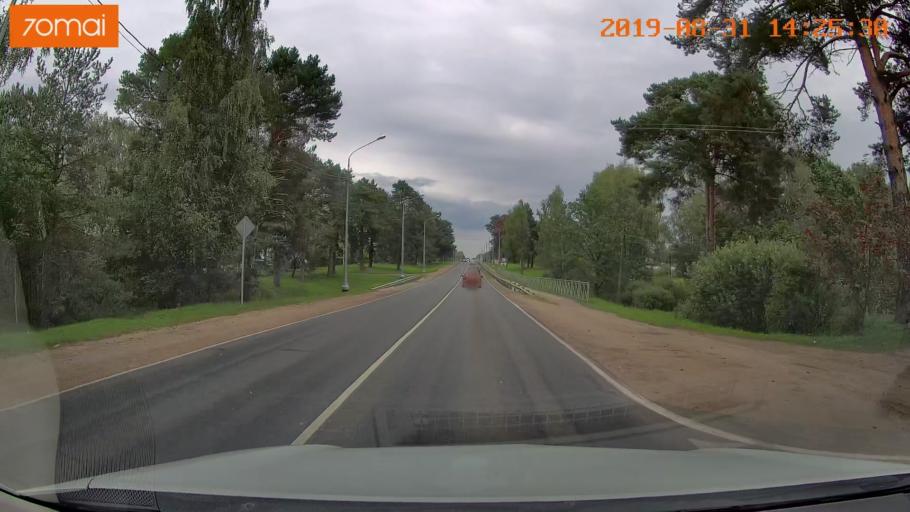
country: RU
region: Smolensk
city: Yekimovichi
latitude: 54.1086
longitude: 33.2743
